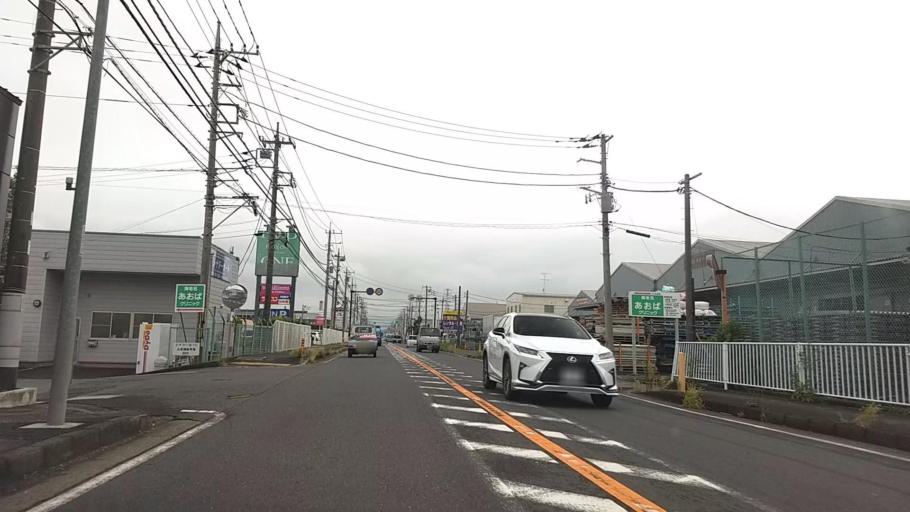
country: JP
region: Kanagawa
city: Atsugi
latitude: 35.4066
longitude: 139.3909
